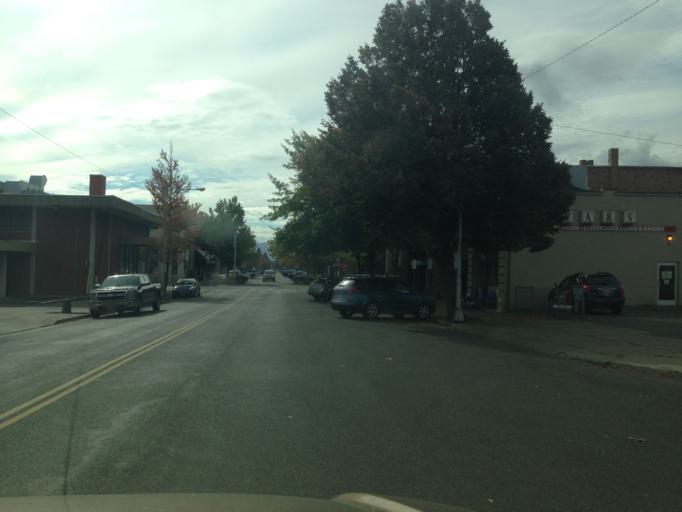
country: US
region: Washington
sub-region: Kittitas County
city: Ellensburg
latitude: 46.9973
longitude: -120.5474
